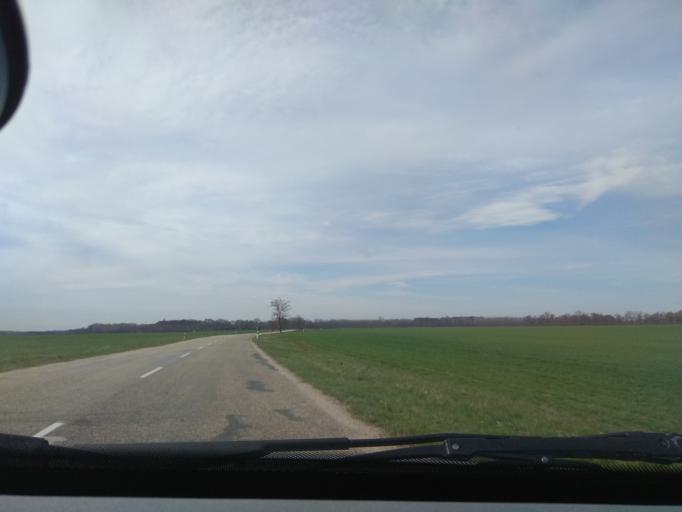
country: SK
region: Trnavsky
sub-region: Okres Dunajska Streda
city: Velky Meder
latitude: 47.8300
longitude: 17.7548
